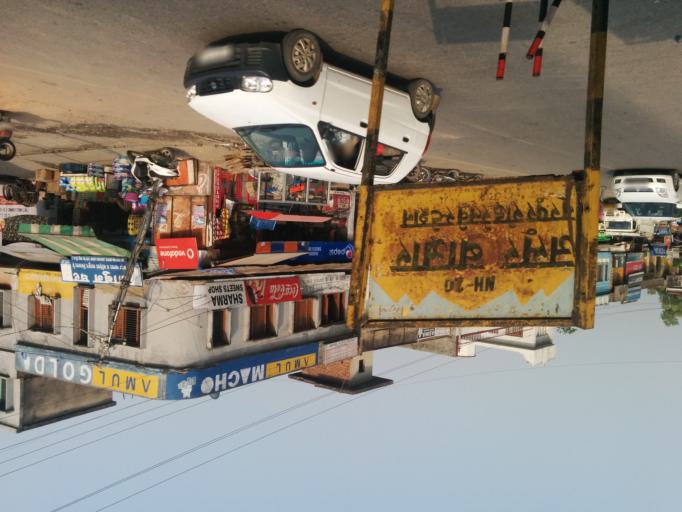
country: IN
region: Punjab
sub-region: Gurdaspur
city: Dharkalan
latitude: 32.2815
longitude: 75.8483
